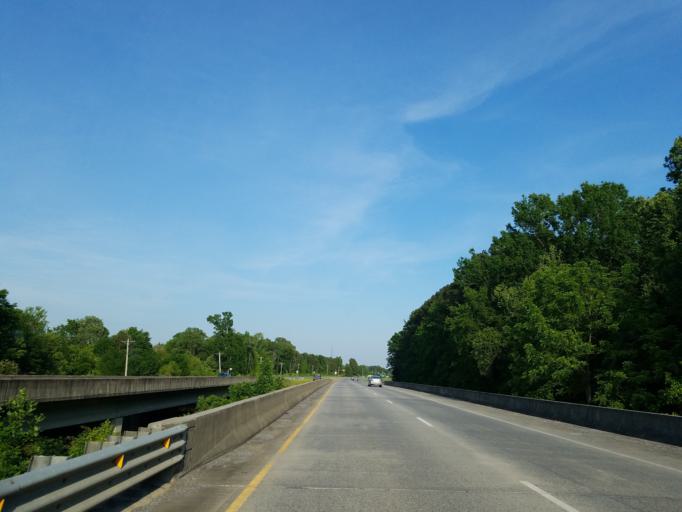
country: US
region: Georgia
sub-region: Floyd County
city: Shannon
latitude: 34.3948
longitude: -85.1972
